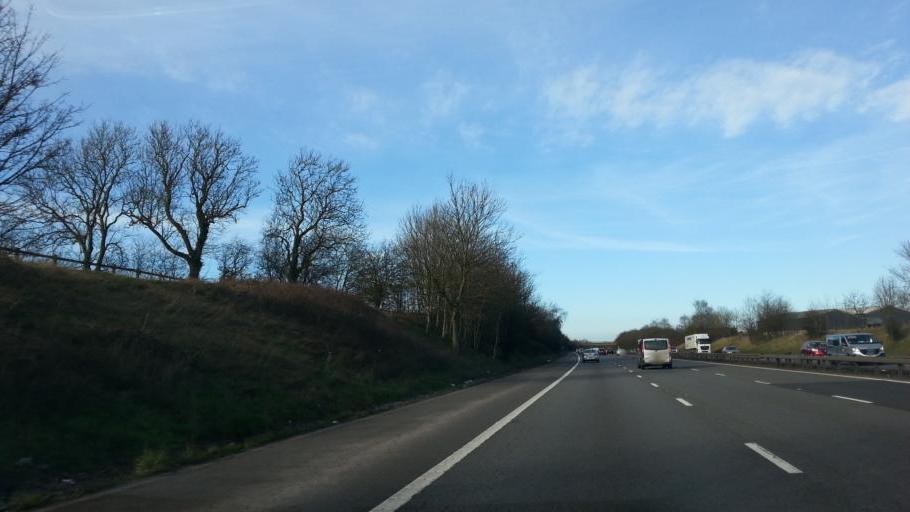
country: GB
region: England
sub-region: Warwickshire
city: Bedworth
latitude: 52.4701
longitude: -1.4059
